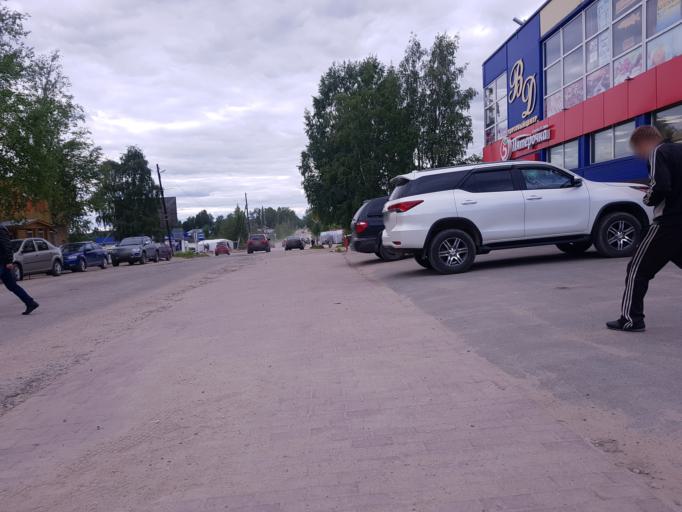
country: RU
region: Republic of Karelia
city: Kalevala
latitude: 65.1975
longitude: 31.1811
